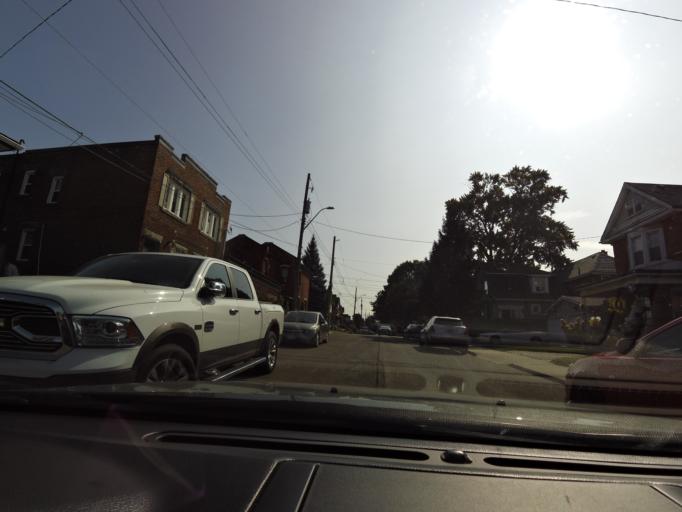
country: CA
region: Ontario
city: Hamilton
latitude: 43.2700
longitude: -79.8576
